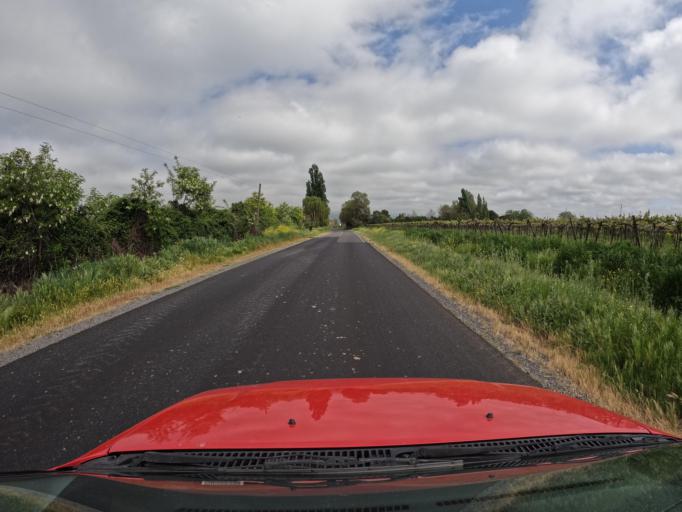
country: CL
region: O'Higgins
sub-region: Provincia de Colchagua
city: Santa Cruz
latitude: -34.6768
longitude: -71.3662
